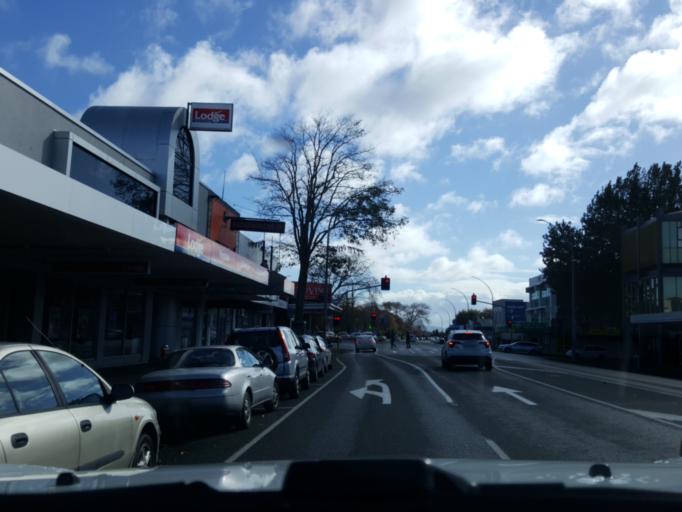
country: NZ
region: Waikato
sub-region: Hamilton City
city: Hamilton
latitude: -37.7804
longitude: 175.2767
